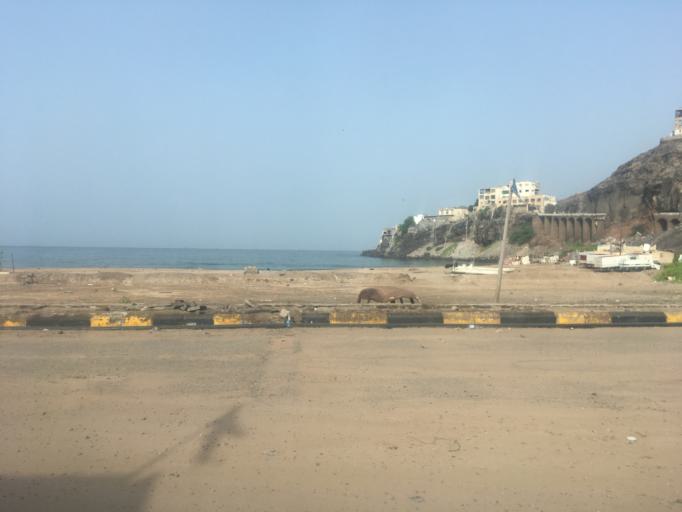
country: YE
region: Aden
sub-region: Attawahi
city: At Tawahi
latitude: 12.7759
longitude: 44.9862
